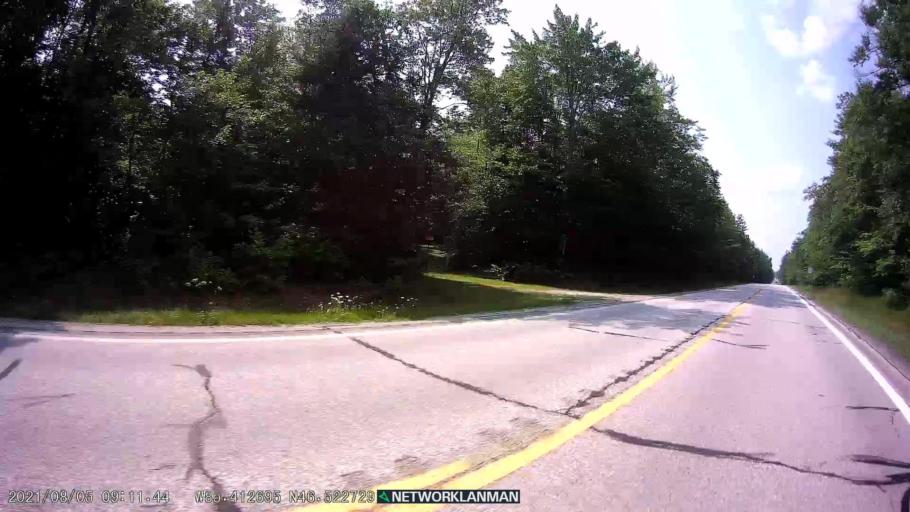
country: US
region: Michigan
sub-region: Luce County
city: Newberry
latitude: 46.5224
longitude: -85.4131
